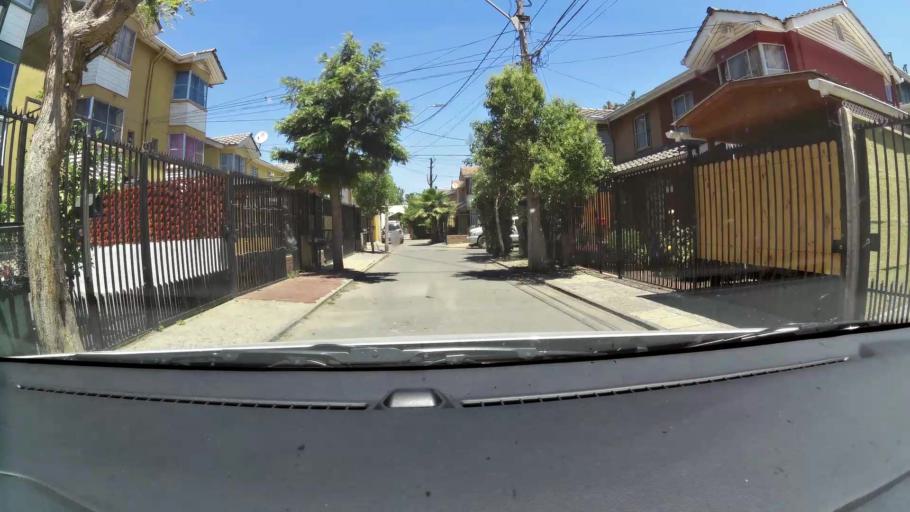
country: CL
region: Santiago Metropolitan
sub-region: Provincia de Maipo
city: San Bernardo
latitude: -33.6033
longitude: -70.6739
